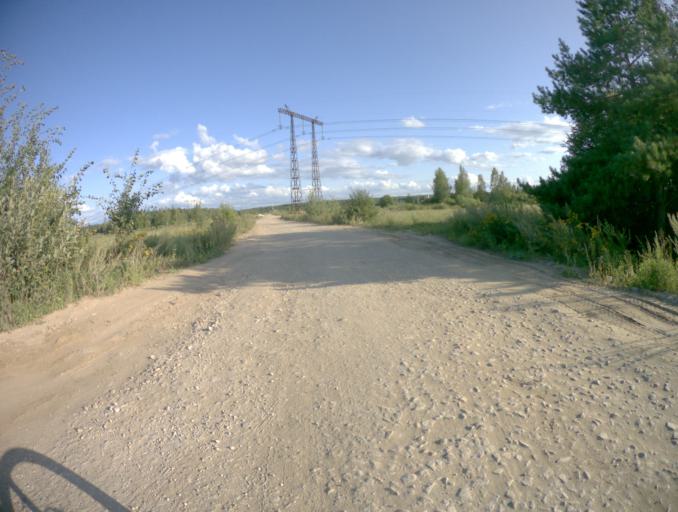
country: RU
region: Vladimir
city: Raduzhnyy
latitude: 56.0823
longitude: 40.2713
